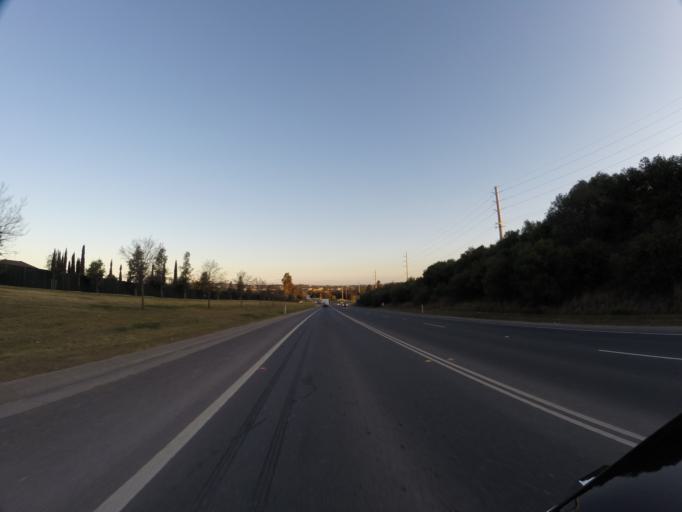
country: AU
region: New South Wales
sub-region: Camden
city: Narellan
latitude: -34.0234
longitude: 150.7263
